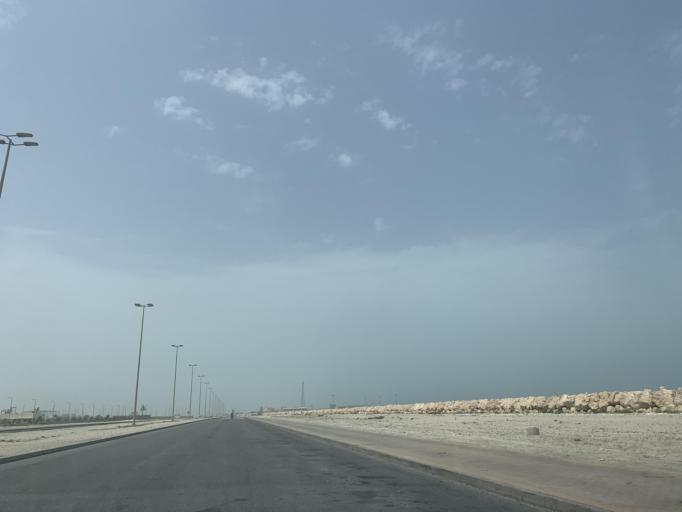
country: BH
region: Muharraq
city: Al Hadd
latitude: 26.2156
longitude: 50.7015
